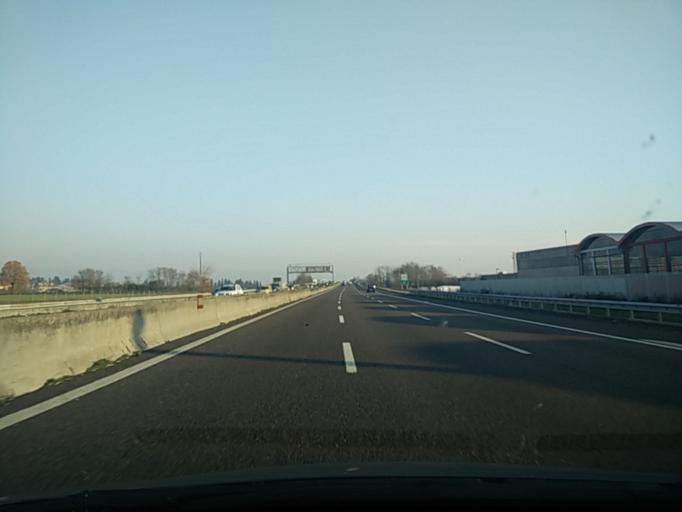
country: IT
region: Lombardy
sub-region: Provincia di Brescia
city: Cazzago San Martino-Calino
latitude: 45.5755
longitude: 10.0155
